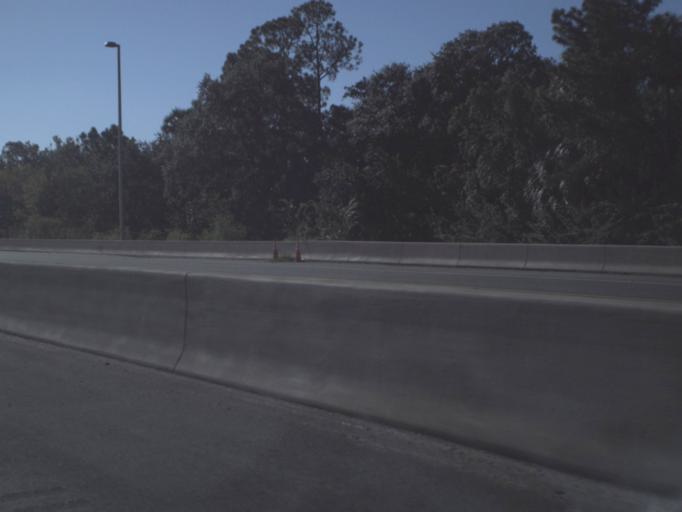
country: US
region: Florida
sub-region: Seminole County
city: Midway
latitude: 28.7424
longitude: -81.2589
